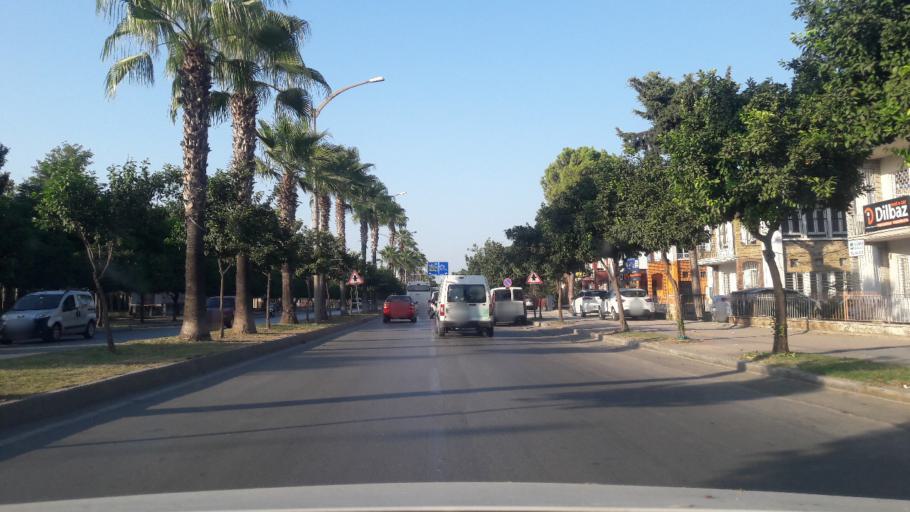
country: TR
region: Adana
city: Seyhan
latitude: 36.9899
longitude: 35.2984
